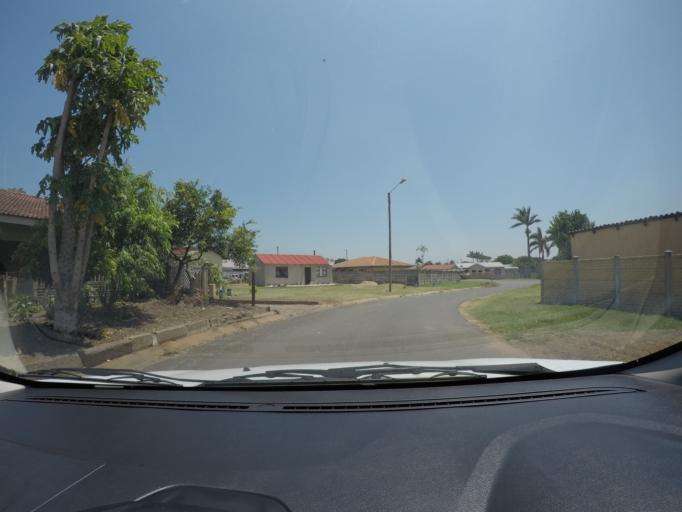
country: ZA
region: KwaZulu-Natal
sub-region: uThungulu District Municipality
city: eSikhawini
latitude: -28.8861
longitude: 31.8878
